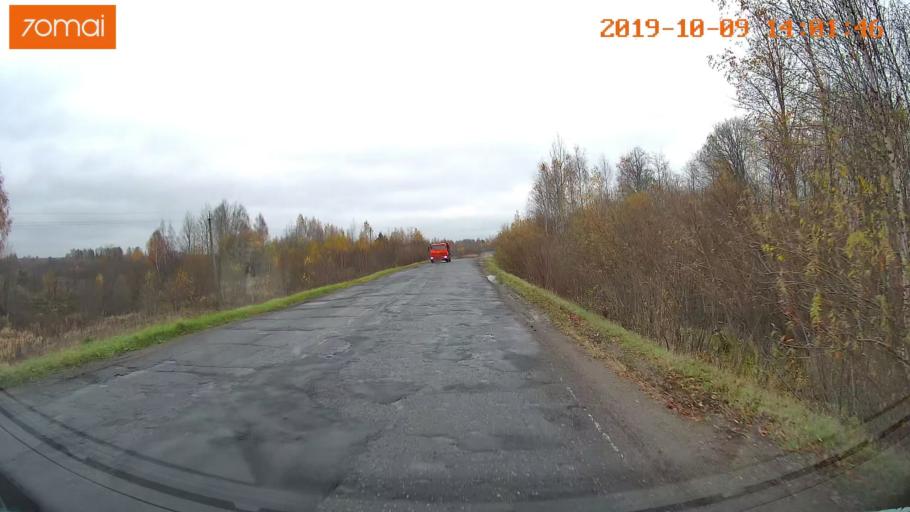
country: RU
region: Kostroma
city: Buy
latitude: 58.4455
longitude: 41.3501
